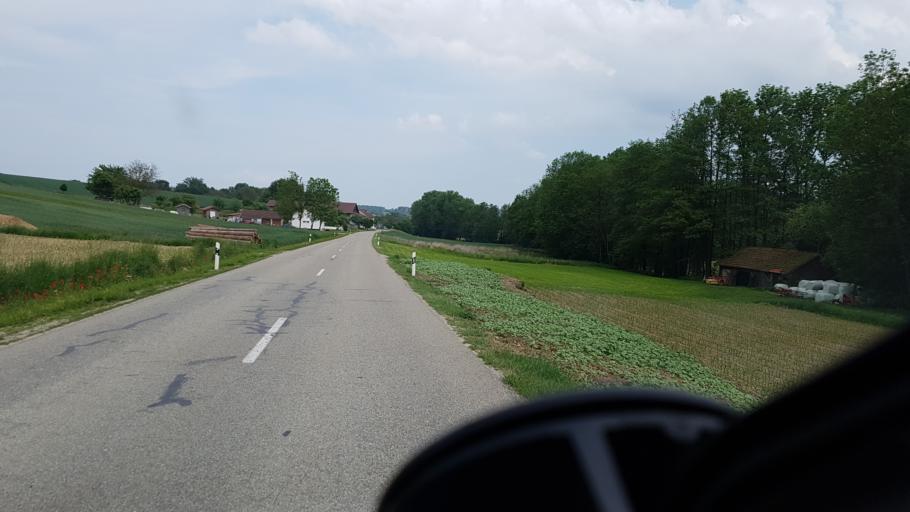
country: DE
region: Bavaria
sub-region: Lower Bavaria
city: Bayerbach
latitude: 48.3922
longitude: 13.1453
